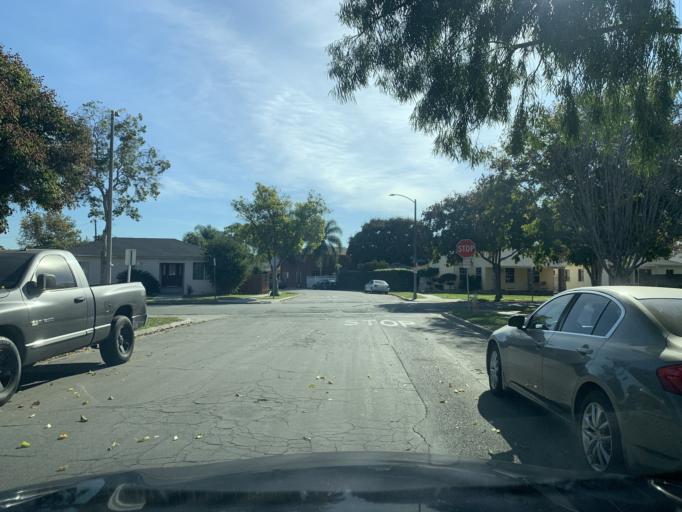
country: US
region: California
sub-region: Los Angeles County
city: East Rancho Dominguez
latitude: 33.8613
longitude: -118.1925
